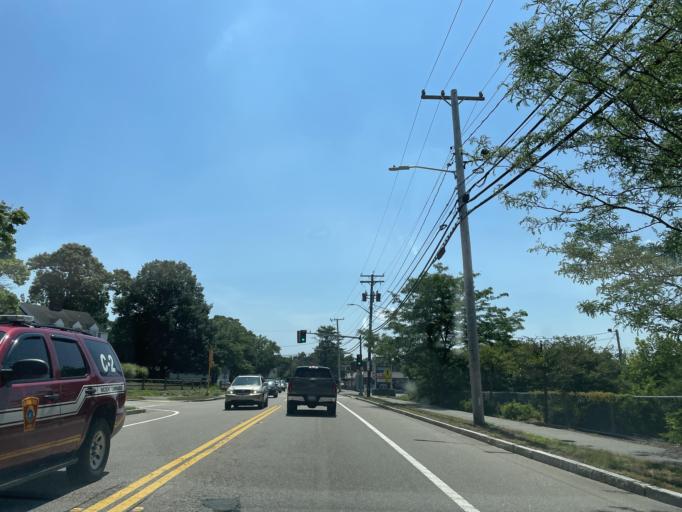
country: US
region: Massachusetts
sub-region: Norfolk County
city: Holbrook
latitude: 42.1819
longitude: -71.0134
